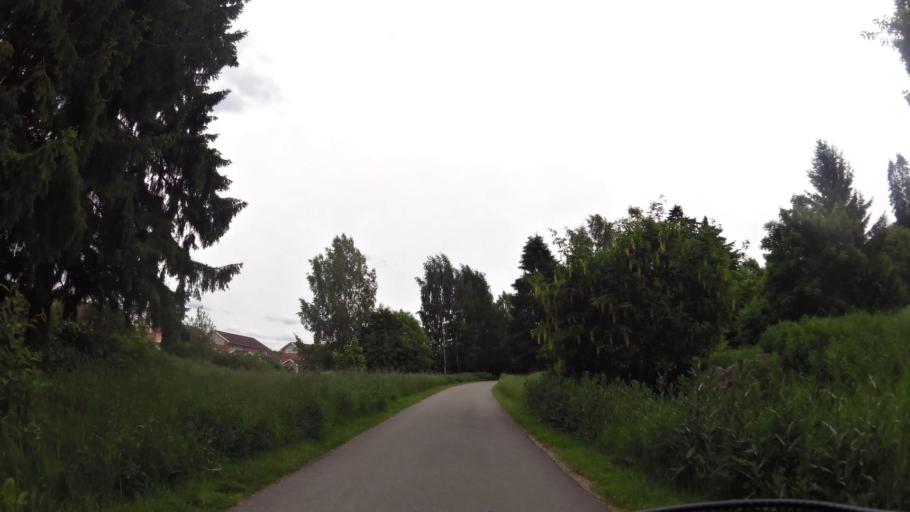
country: SE
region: OEstergoetland
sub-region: Linkopings Kommun
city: Malmslatt
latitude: 58.3790
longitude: 15.5631
